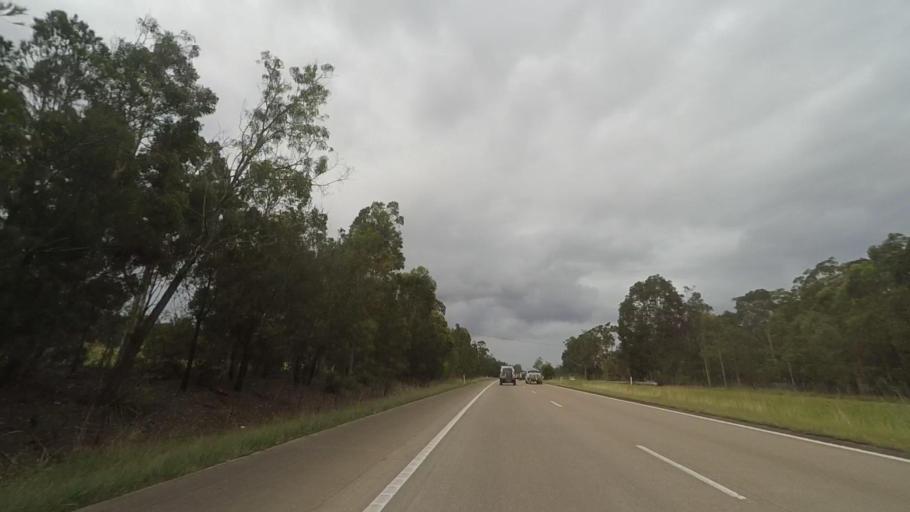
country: AU
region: New South Wales
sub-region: Port Stephens Shire
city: Raymond Terrace
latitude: -32.7204
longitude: 151.7891
